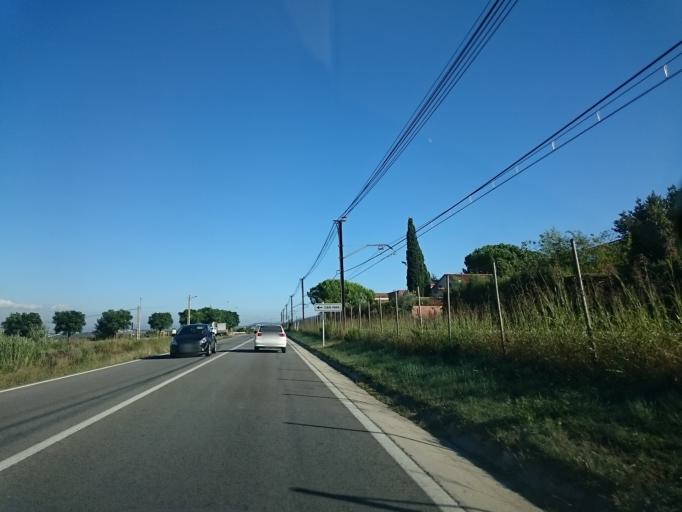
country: ES
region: Catalonia
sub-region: Provincia de Barcelona
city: Piera
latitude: 41.5164
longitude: 1.7636
